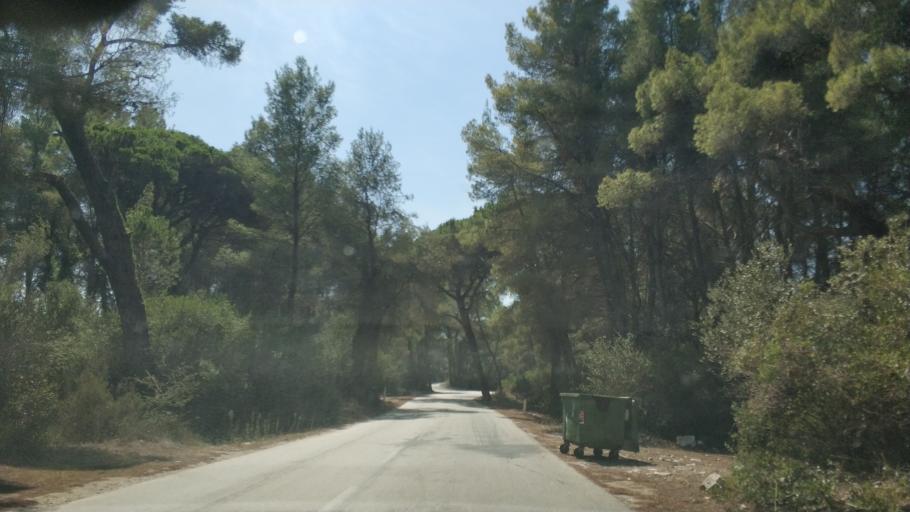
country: AL
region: Fier
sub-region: Rrethi i Lushnjes
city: Divjake
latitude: 40.9812
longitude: 19.4823
